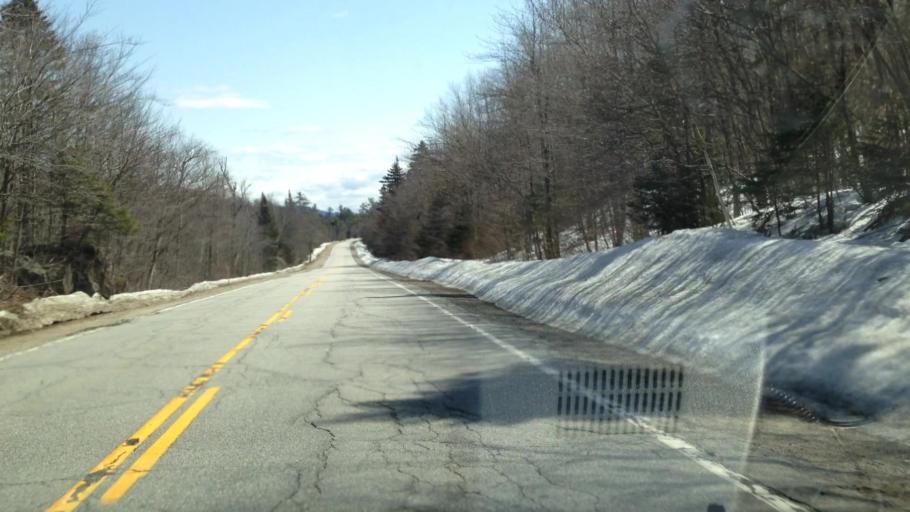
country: US
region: New Hampshire
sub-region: Sullivan County
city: Springfield
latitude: 43.4959
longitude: -72.0024
